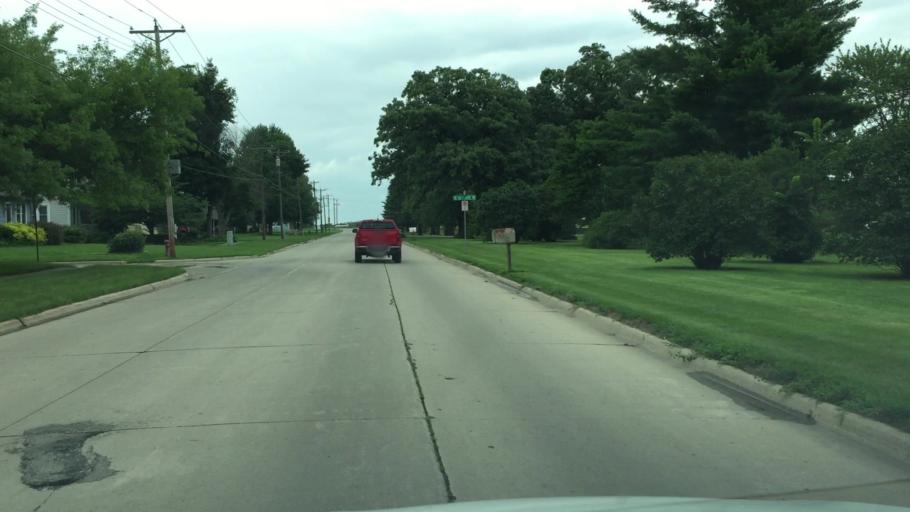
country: US
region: Iowa
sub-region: Jasper County
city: Newton
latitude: 41.7143
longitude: -93.0532
